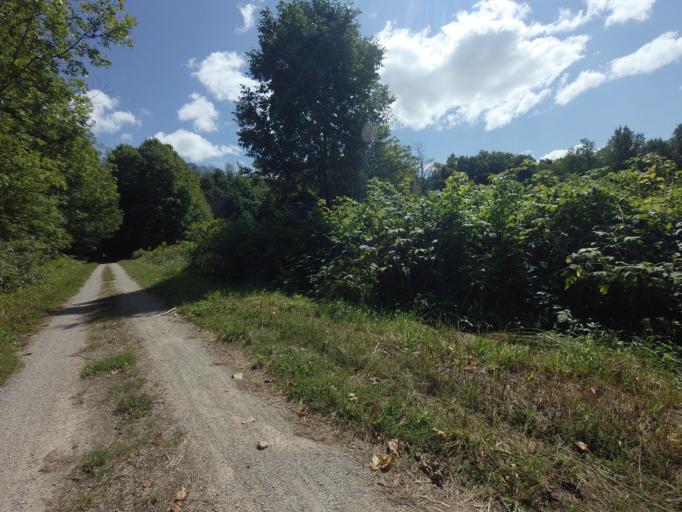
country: CA
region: Ontario
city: Orangeville
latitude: 43.7894
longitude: -80.2554
